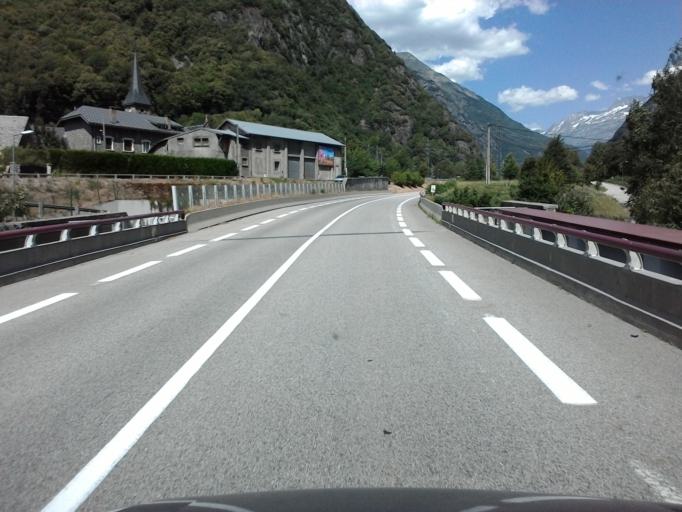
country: FR
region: Rhone-Alpes
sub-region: Departement de l'Isere
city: Livet-et-Gavet
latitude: 45.1071
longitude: 5.9353
